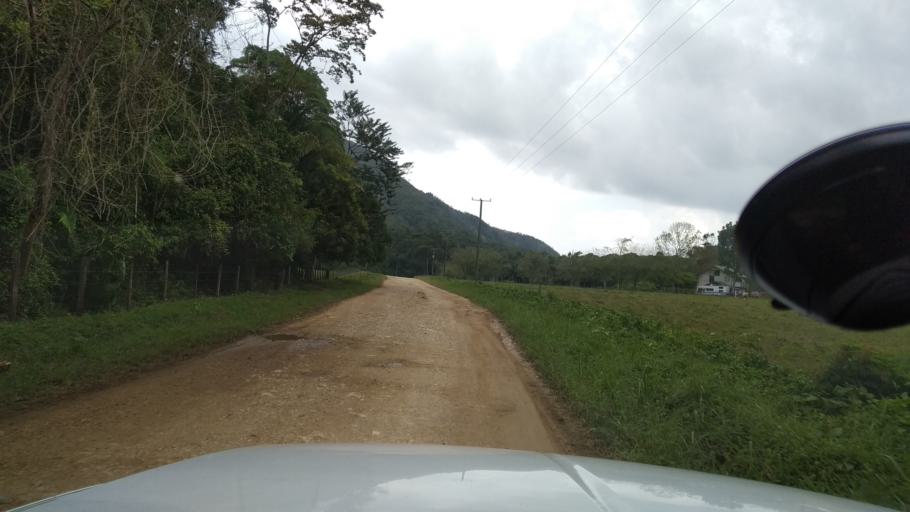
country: BZ
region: Toledo
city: Punta Gorda
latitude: 16.2091
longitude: -89.0246
